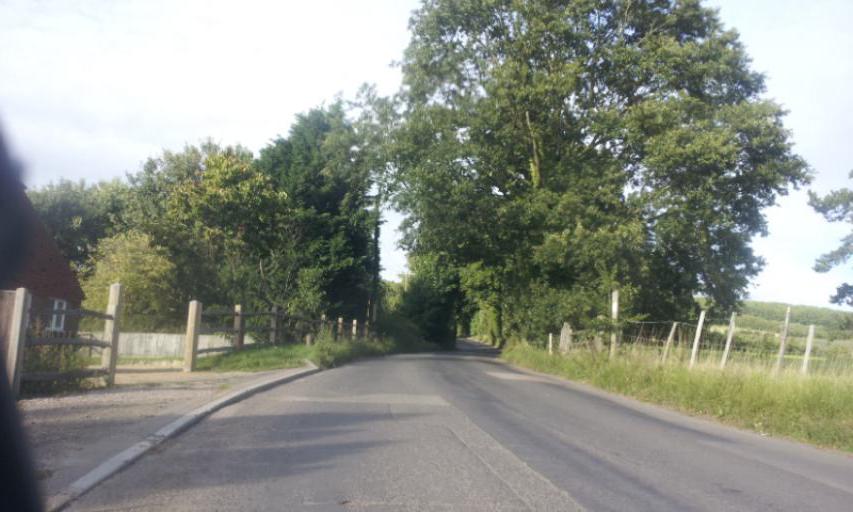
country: GB
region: England
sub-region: Kent
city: Yalding
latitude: 51.2252
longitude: 0.4721
